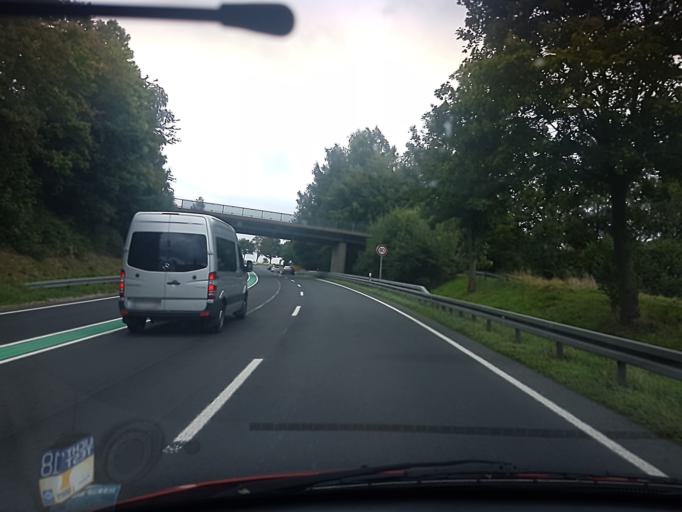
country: DE
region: Bavaria
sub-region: Upper Franconia
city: Bad Alexandersbad
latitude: 50.0200
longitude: 12.0252
